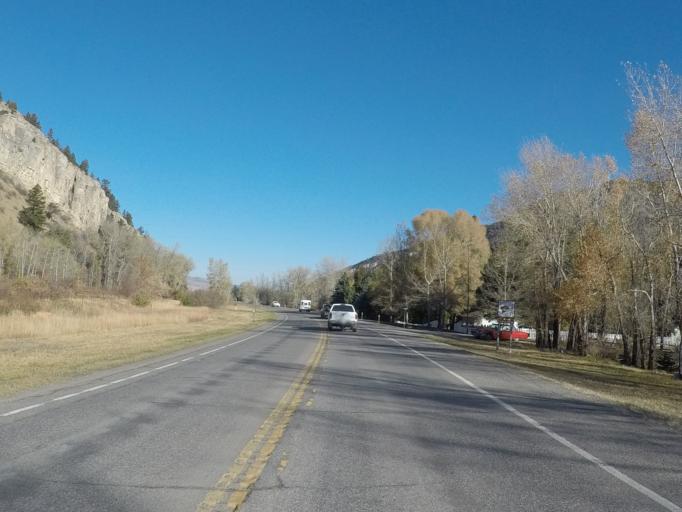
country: US
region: Montana
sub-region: Park County
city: Livingston
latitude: 45.5940
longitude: -110.5710
